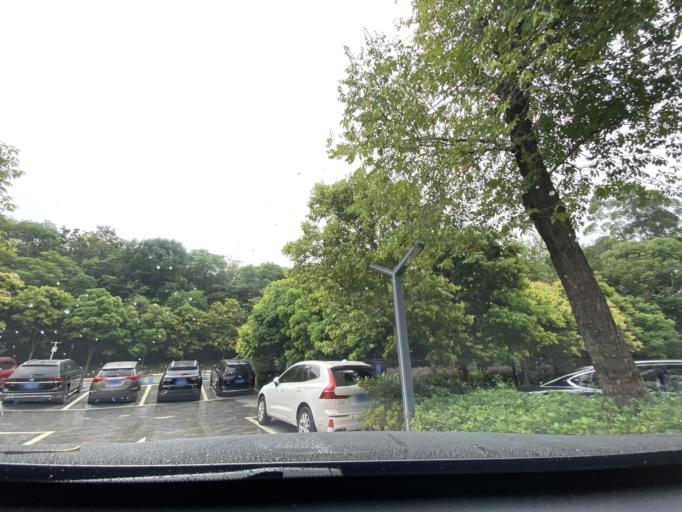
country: CN
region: Sichuan
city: Longquan
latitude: 30.6073
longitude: 104.4765
